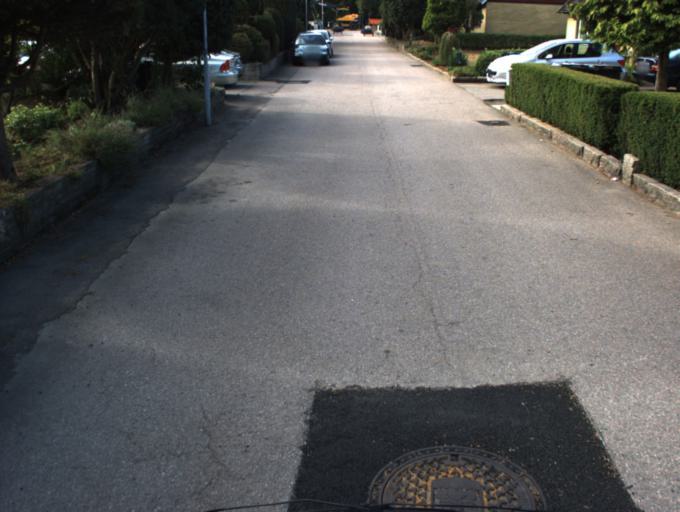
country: SE
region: Skane
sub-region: Helsingborg
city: Barslov
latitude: 56.0350
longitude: 12.8255
